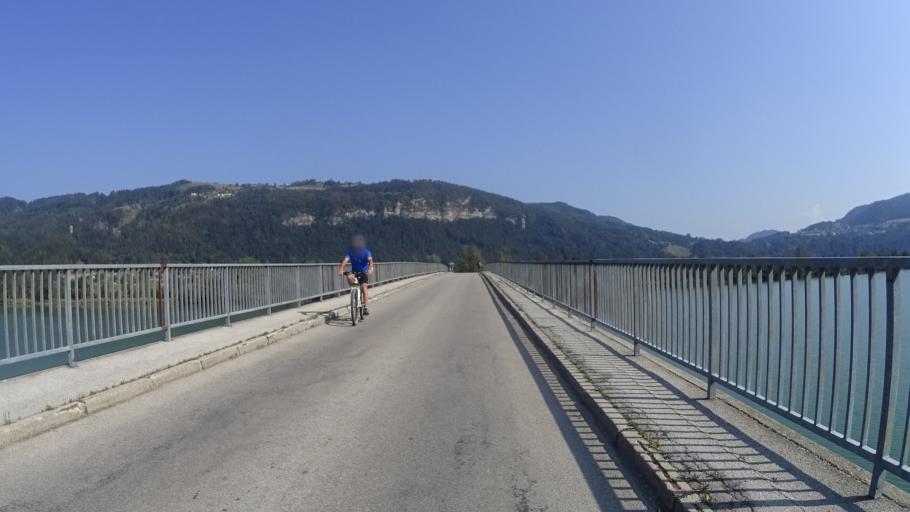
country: AT
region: Carinthia
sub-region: Politischer Bezirk Klagenfurt Land
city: Grafenstein
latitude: 46.5566
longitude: 14.4166
